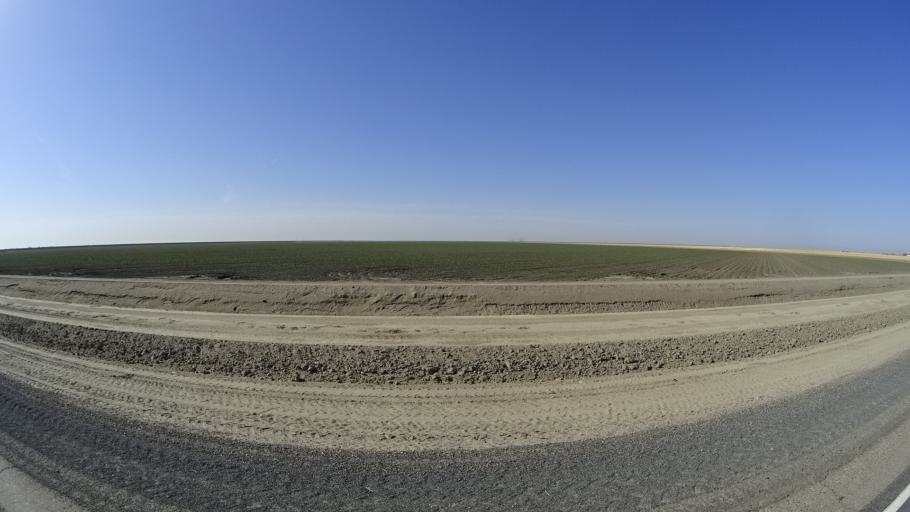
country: US
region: California
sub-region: Kings County
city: Corcoran
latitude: 36.0980
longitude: -119.6151
